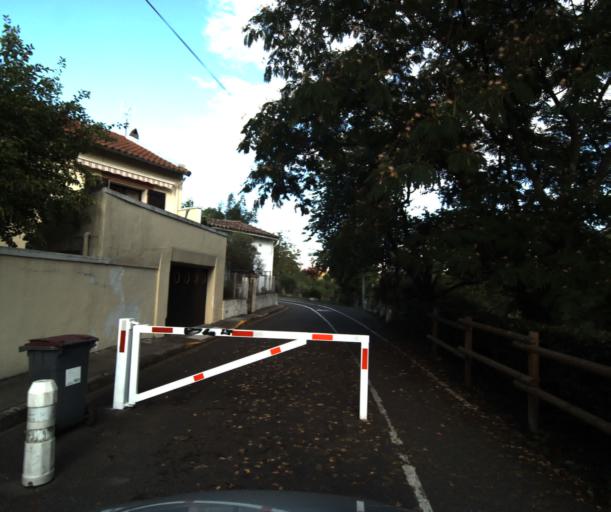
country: FR
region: Midi-Pyrenees
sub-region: Departement de la Haute-Garonne
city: Muret
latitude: 43.4622
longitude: 1.3261
